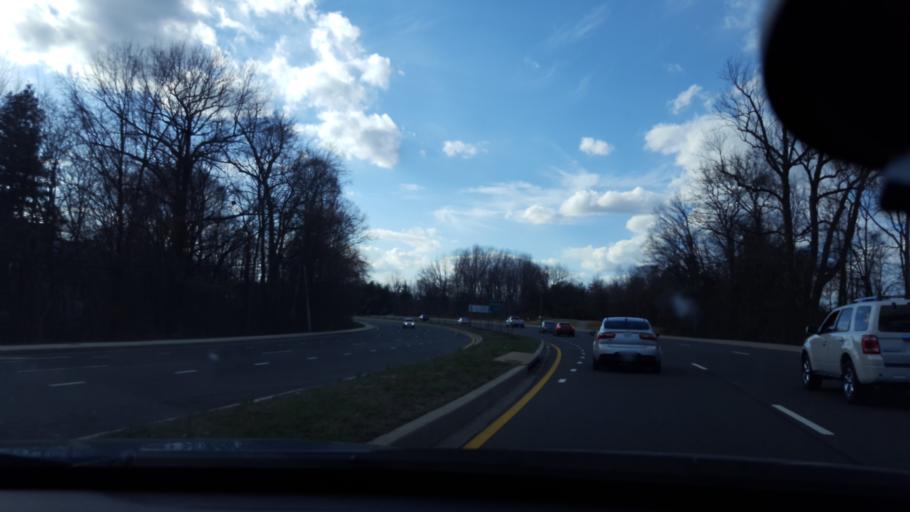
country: US
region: Maryland
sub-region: Prince George's County
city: Bowie
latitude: 38.9457
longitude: -76.7247
